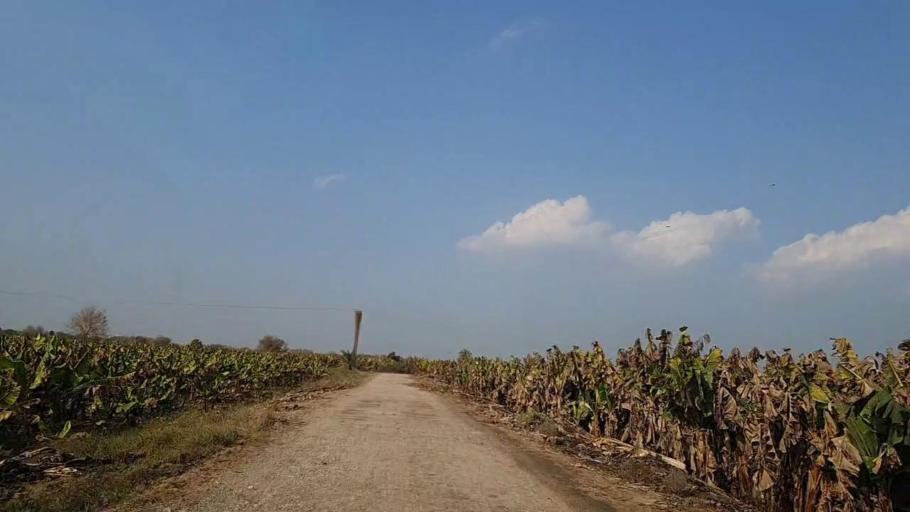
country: PK
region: Sindh
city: Nawabshah
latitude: 26.1516
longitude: 68.4005
